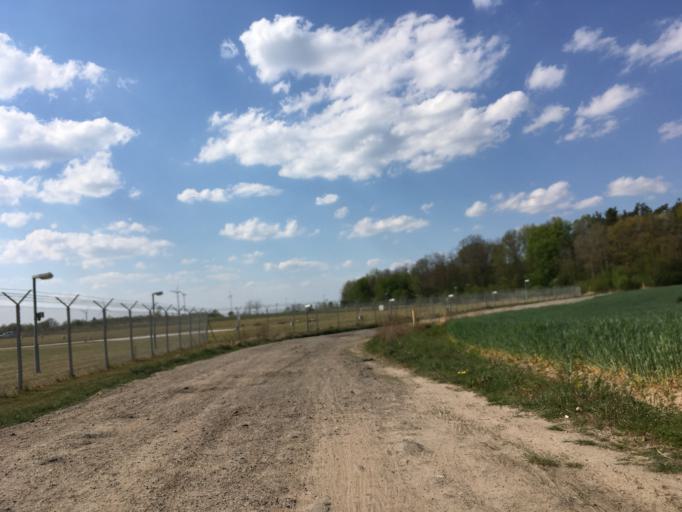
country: DE
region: Brandenburg
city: Ahrensfelde
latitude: 52.6014
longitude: 13.5777
